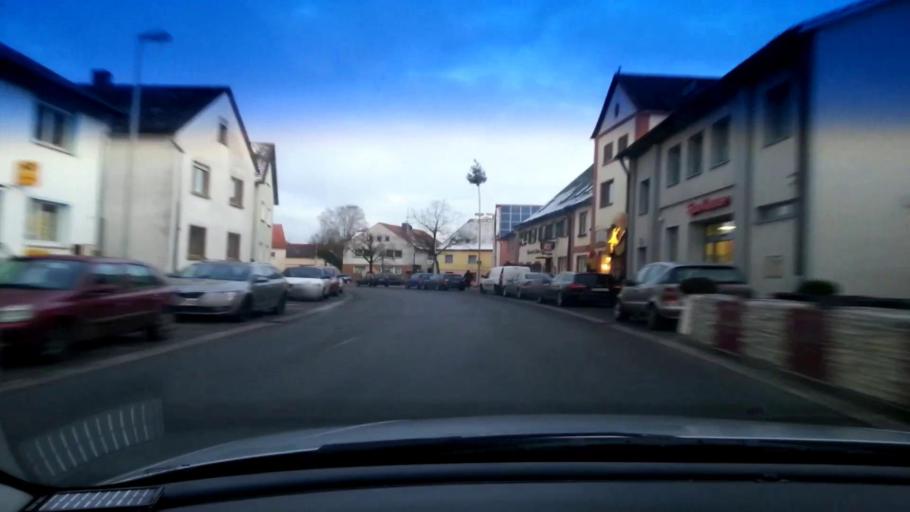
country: DE
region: Bavaria
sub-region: Upper Franconia
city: Frensdorf
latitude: 49.8172
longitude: 10.8653
